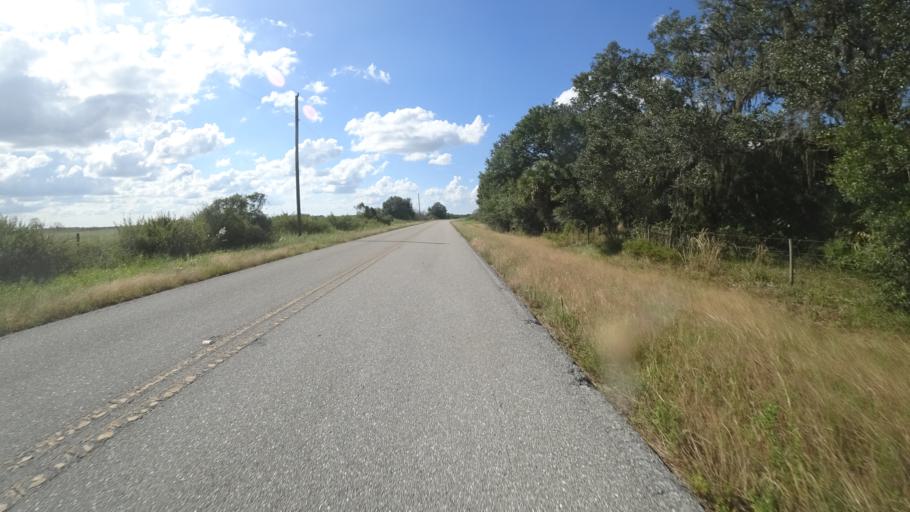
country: US
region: Florida
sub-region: DeSoto County
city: Nocatee
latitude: 27.2690
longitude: -82.0912
